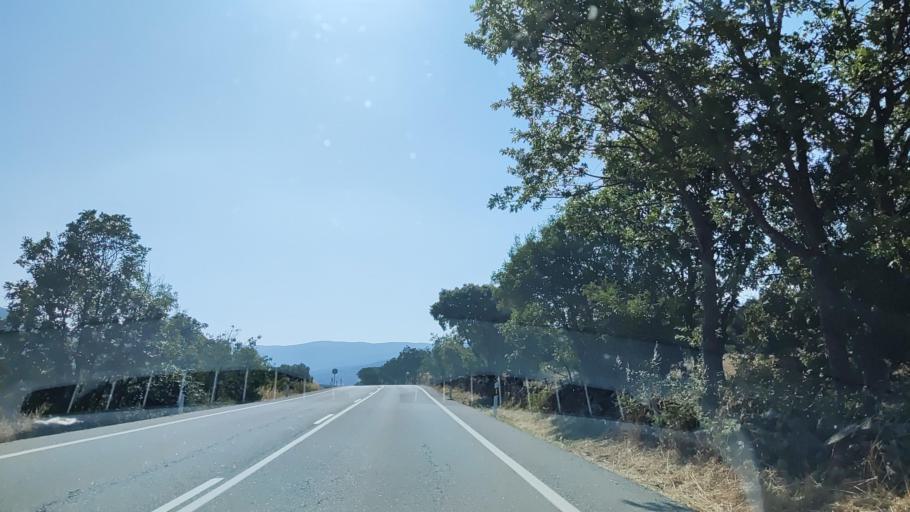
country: ES
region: Madrid
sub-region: Provincia de Madrid
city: Lozoya
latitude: 40.9469
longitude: -3.7517
